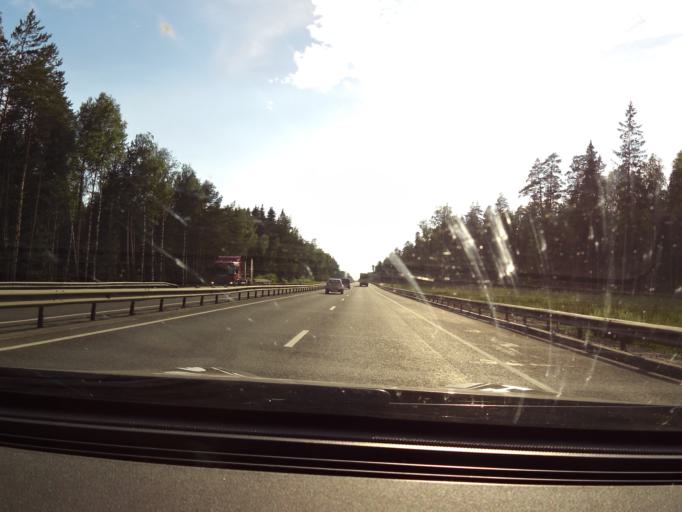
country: RU
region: Vladimir
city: Krasnyy Oktyabr'
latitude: 56.2173
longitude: 41.4365
